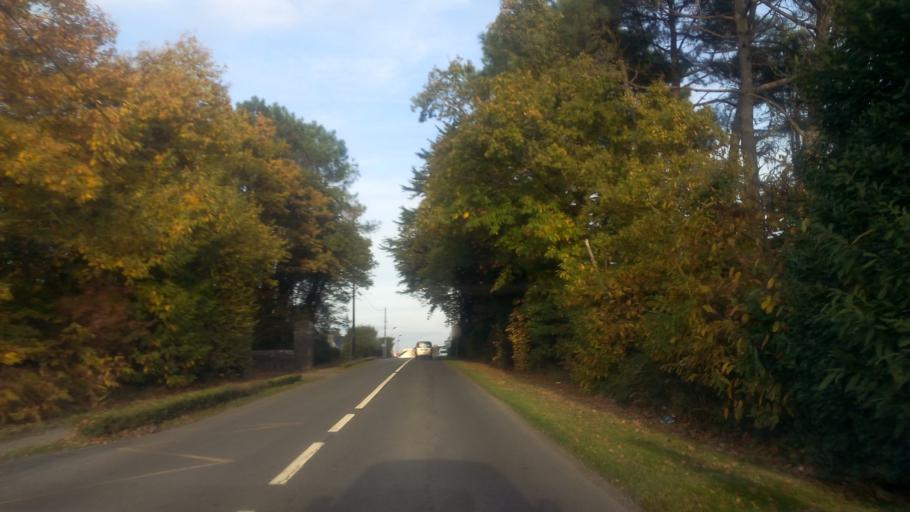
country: FR
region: Pays de la Loire
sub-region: Departement de la Loire-Atlantique
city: Avessac
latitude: 47.6496
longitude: -1.9946
